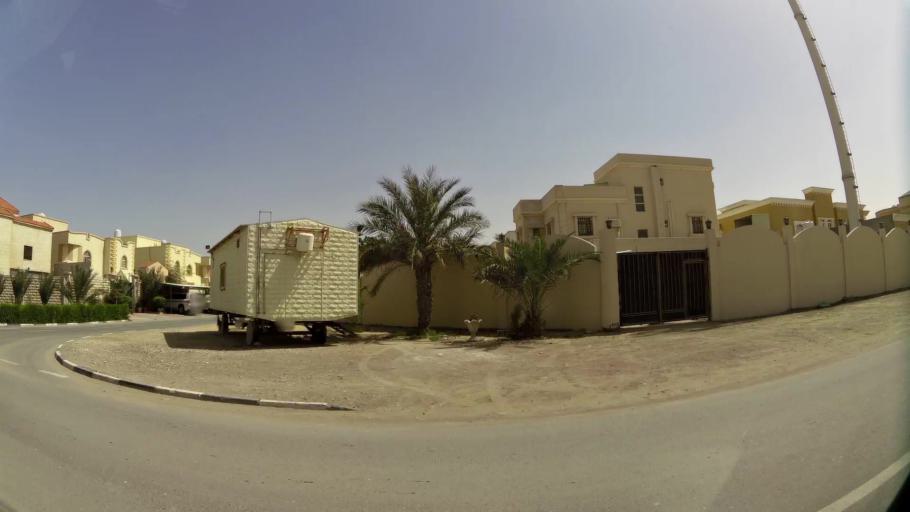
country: QA
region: Baladiyat Umm Salal
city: Umm Salal Muhammad
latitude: 25.3903
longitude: 51.4188
